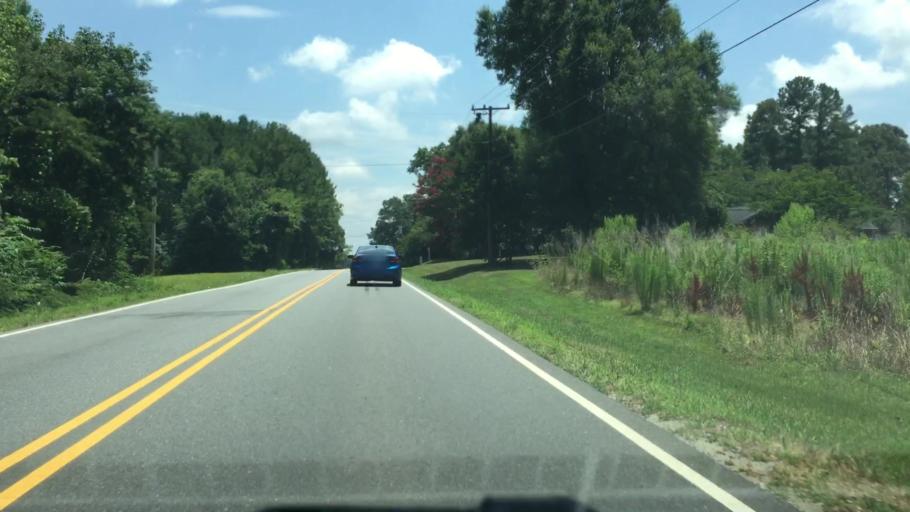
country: US
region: North Carolina
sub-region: Rowan County
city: Enochville
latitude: 35.4717
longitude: -80.7450
